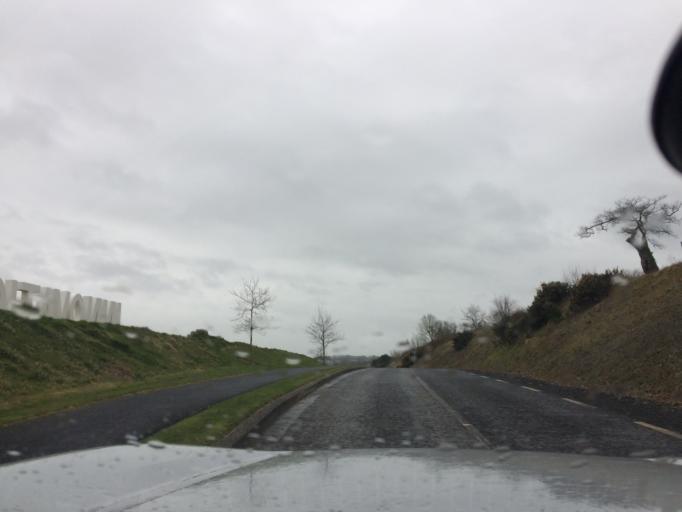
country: IE
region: Leinster
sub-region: Kilkenny
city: Mooncoin
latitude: 52.2532
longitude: -7.1849
